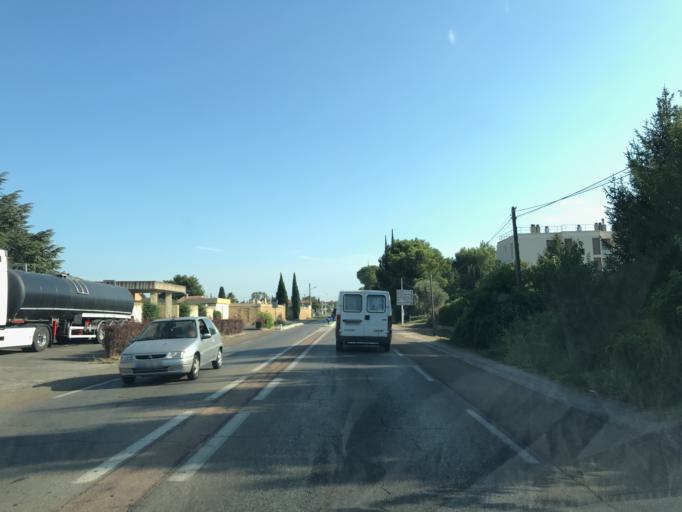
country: FR
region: Provence-Alpes-Cote d'Azur
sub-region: Departement des Bouches-du-Rhone
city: Saint-Chamas
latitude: 43.5468
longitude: 5.0411
